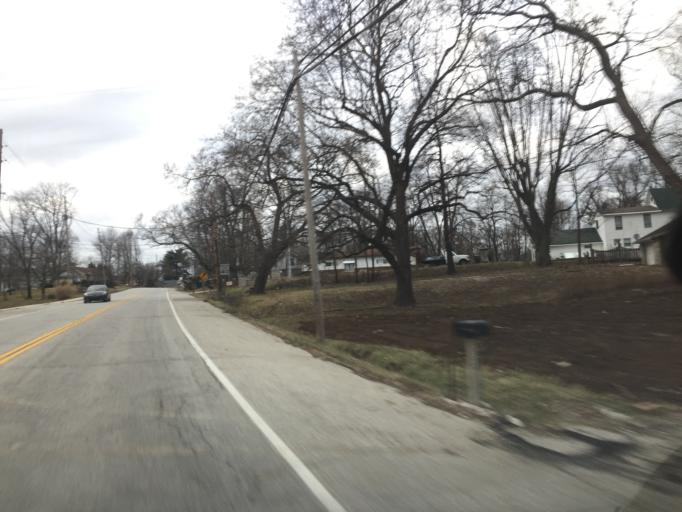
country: US
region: Indiana
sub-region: Monroe County
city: Bloomington
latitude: 39.1803
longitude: -86.5487
